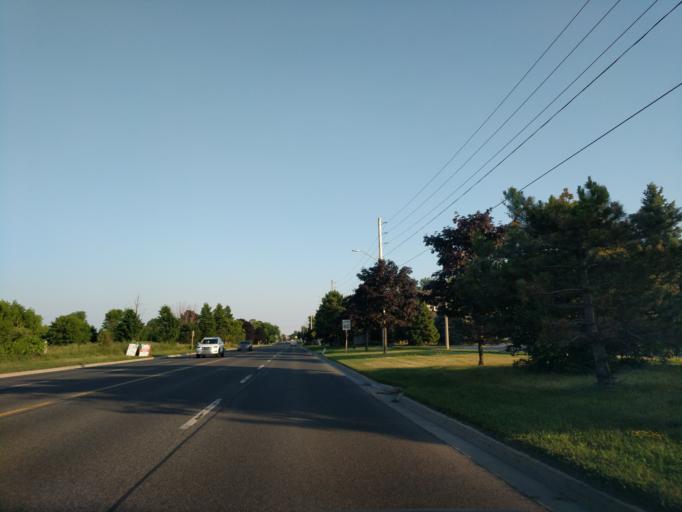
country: CA
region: Ontario
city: Oshawa
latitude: 43.9140
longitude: -78.9030
